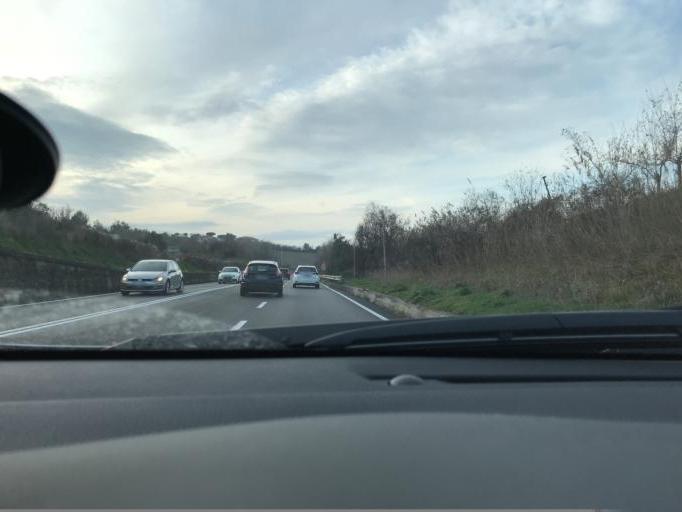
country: IT
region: The Marches
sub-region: Provincia di Ancona
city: Posatora
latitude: 43.5968
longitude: 13.4443
